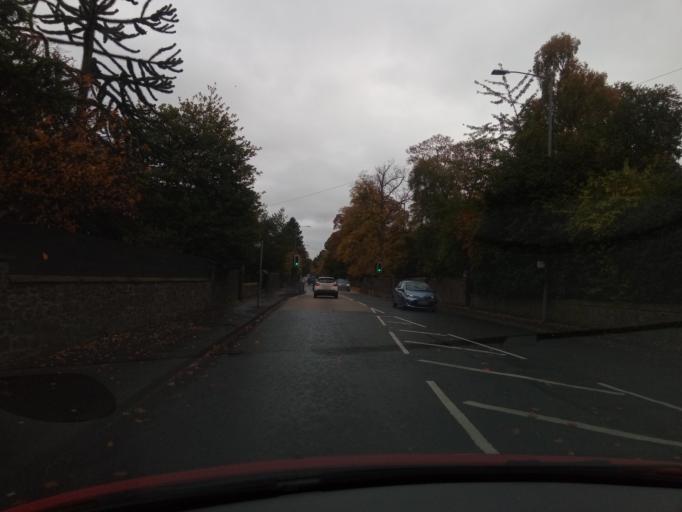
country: GB
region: Scotland
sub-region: The Scottish Borders
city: Galashiels
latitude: 55.6114
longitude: -2.8017
